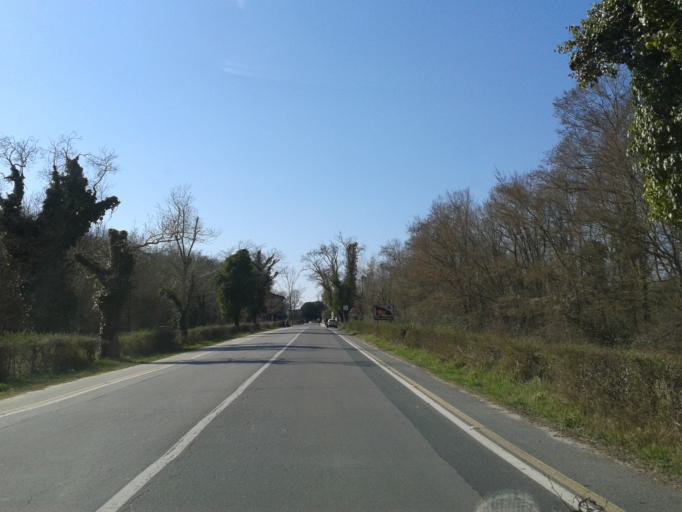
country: IT
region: Tuscany
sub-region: Province of Pisa
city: Madonna dell'Acqua
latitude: 43.7227
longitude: 10.3465
